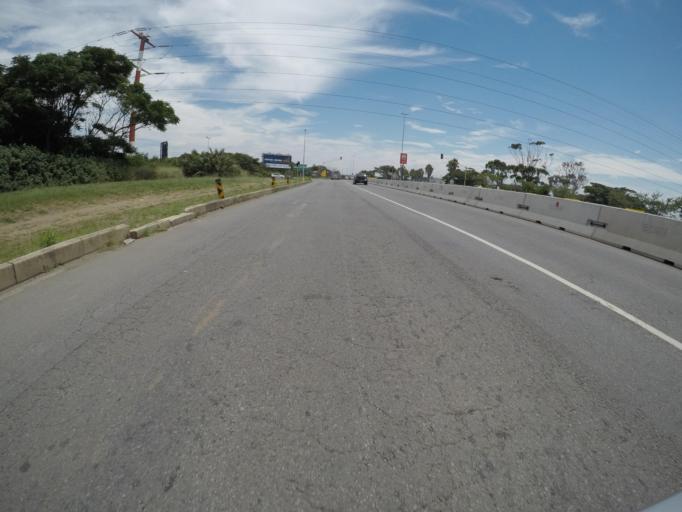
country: ZA
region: Eastern Cape
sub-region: Buffalo City Metropolitan Municipality
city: East London
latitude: -33.0355
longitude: 27.8481
